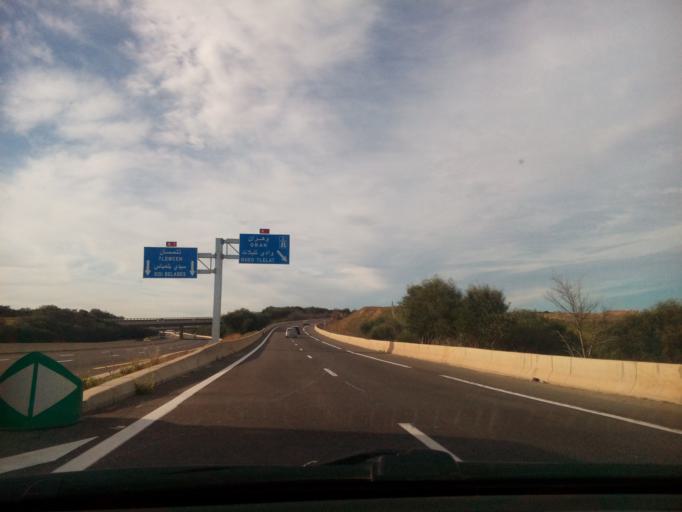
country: DZ
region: Mascara
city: Sig
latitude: 35.5439
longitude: -0.3414
